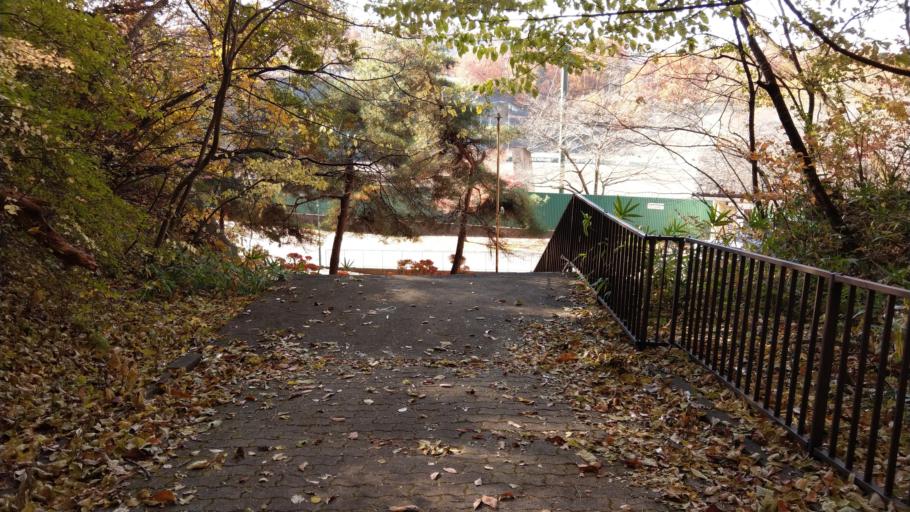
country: JP
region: Nagano
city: Komoro
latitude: 36.3176
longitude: 138.4244
